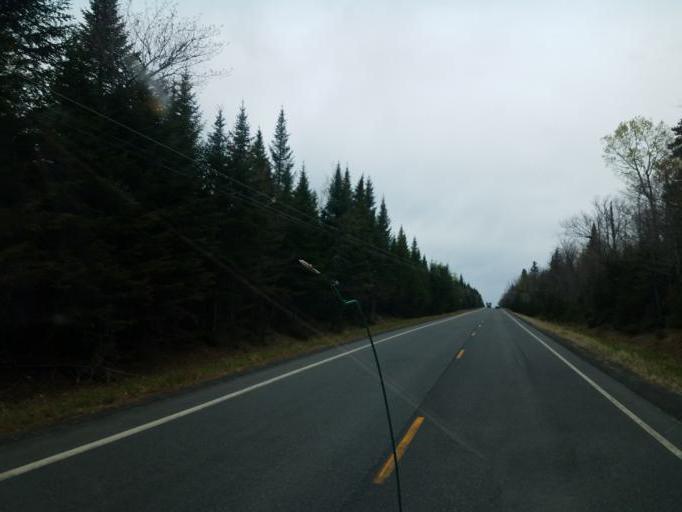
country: US
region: Maine
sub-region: Penobscot County
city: Patten
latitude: 46.2935
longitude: -68.3575
